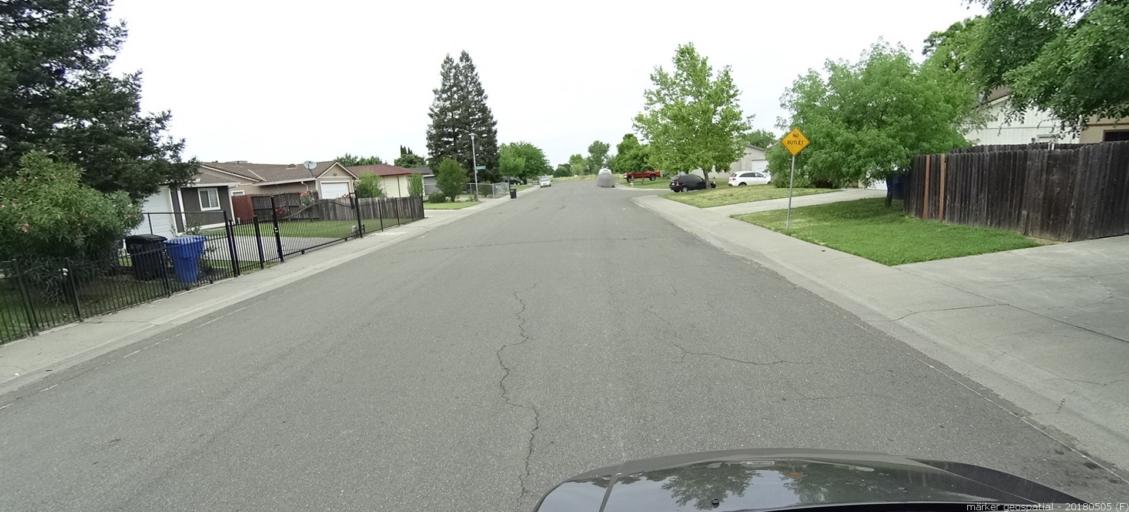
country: US
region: California
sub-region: Sacramento County
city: Rio Linda
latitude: 38.6494
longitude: -121.4603
